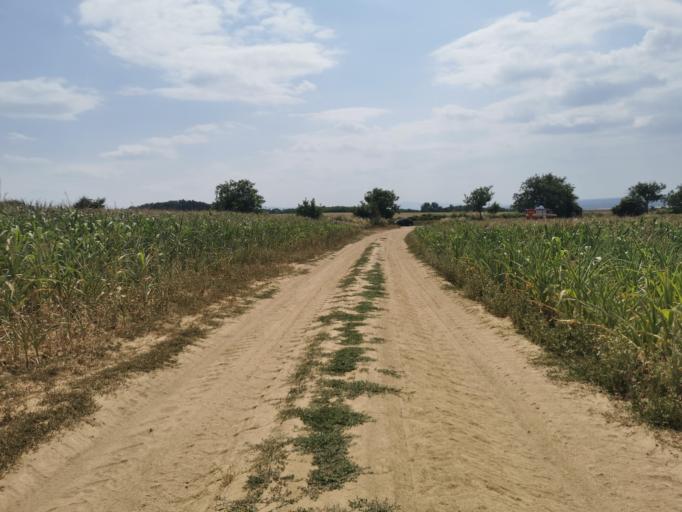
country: SK
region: Trnavsky
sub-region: Okres Senica
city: Senica
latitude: 48.6792
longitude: 17.4257
